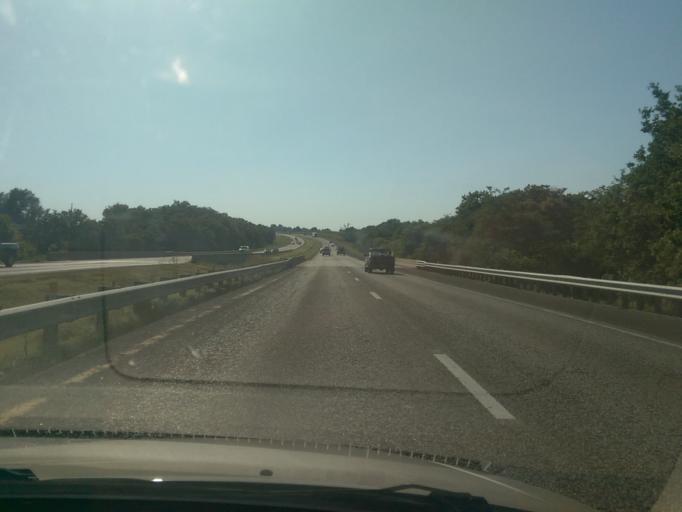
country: US
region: Missouri
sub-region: Lafayette County
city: Concordia
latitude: 38.9906
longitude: -93.6447
